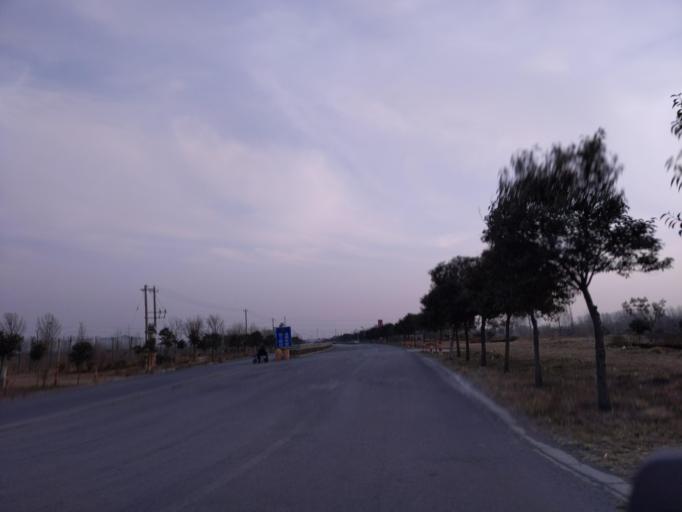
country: CN
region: Henan Sheng
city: Puyang
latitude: 35.8120
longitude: 114.9665
